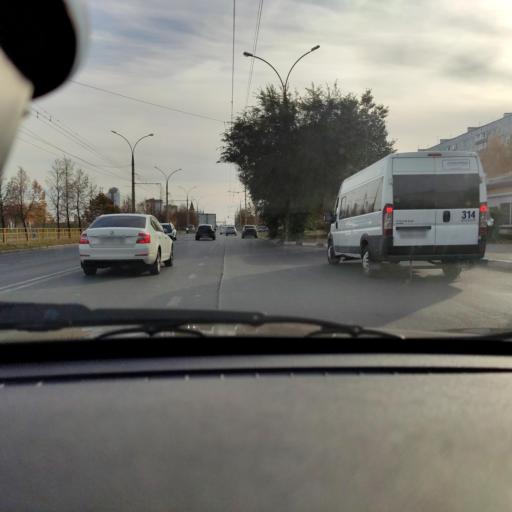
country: RU
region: Samara
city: Tol'yatti
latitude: 53.5104
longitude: 49.2715
